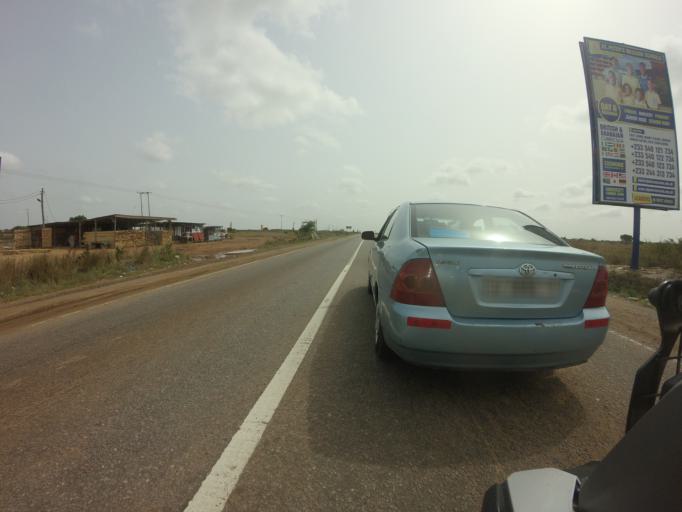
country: GH
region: Greater Accra
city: Tema
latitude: 5.7768
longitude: 0.0843
